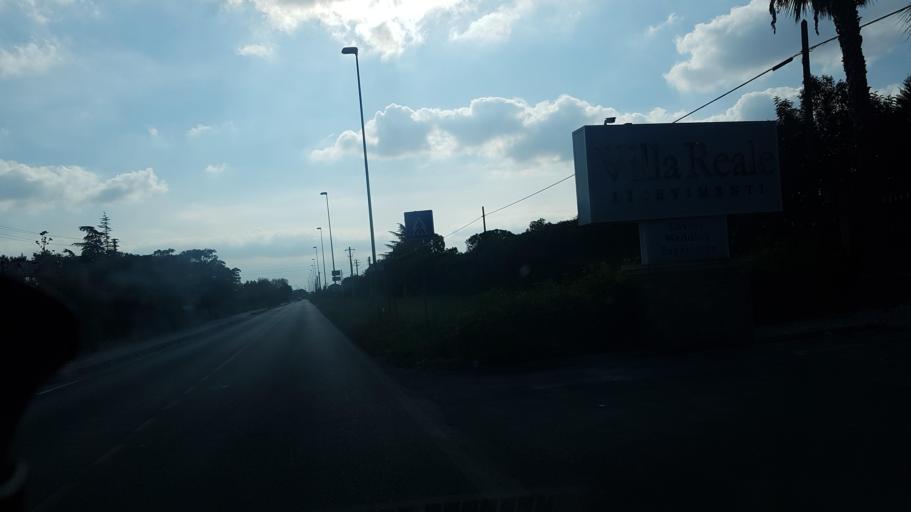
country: IT
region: Apulia
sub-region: Provincia di Foggia
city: Foggia
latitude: 41.4425
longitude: 15.5251
